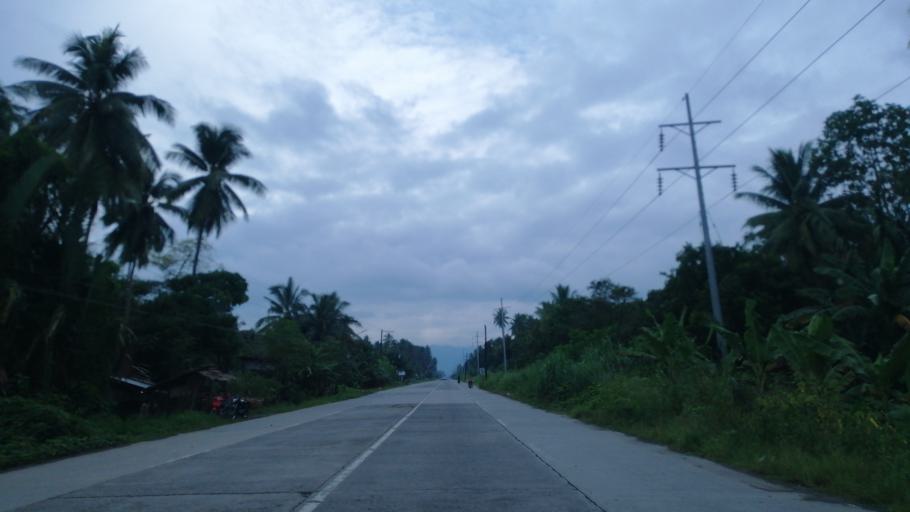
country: PH
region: Davao
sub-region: Province of Davao del Norte
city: Corocotan
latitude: 7.3947
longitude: 125.7831
